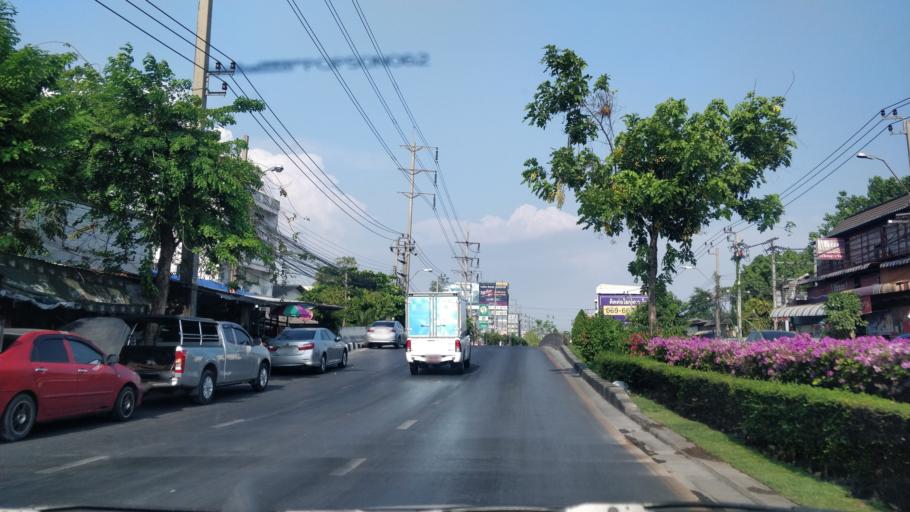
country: TH
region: Bangkok
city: Suan Luang
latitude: 13.7201
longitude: 100.6778
